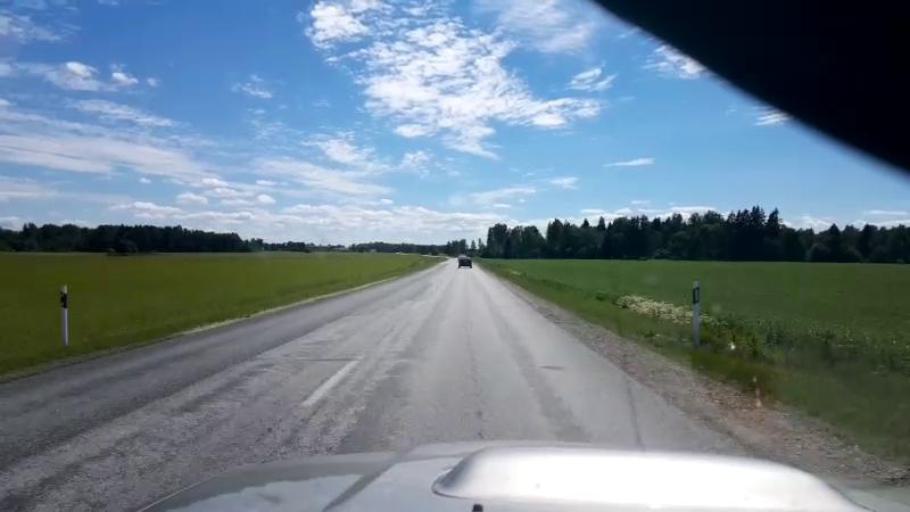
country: EE
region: Jogevamaa
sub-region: Jogeva linn
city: Jogeva
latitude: 58.8297
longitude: 26.2870
